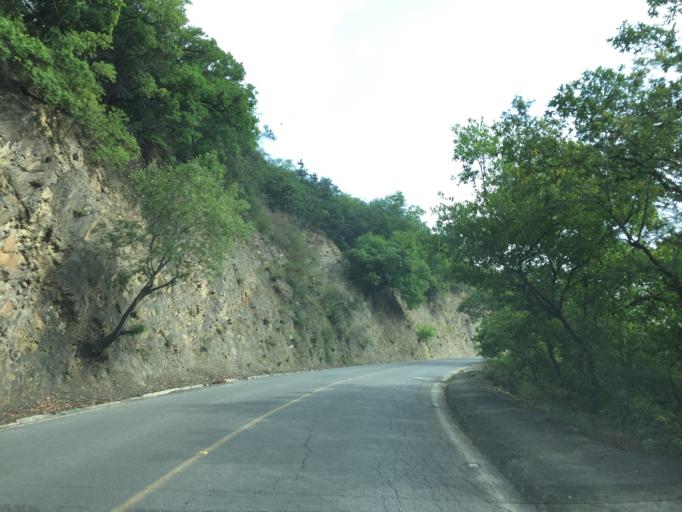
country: MX
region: Nuevo Leon
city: Garza Garcia
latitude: 25.6179
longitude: -100.3627
